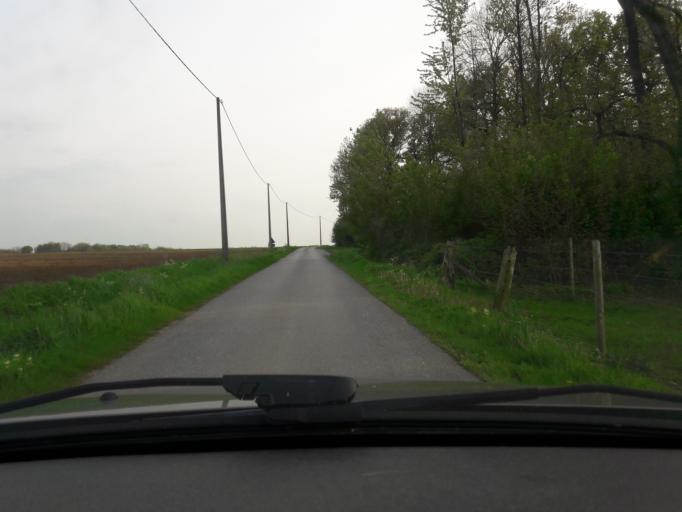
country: FR
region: Nord-Pas-de-Calais
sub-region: Departement du Nord
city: Marpent
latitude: 50.2462
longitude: 4.0798
